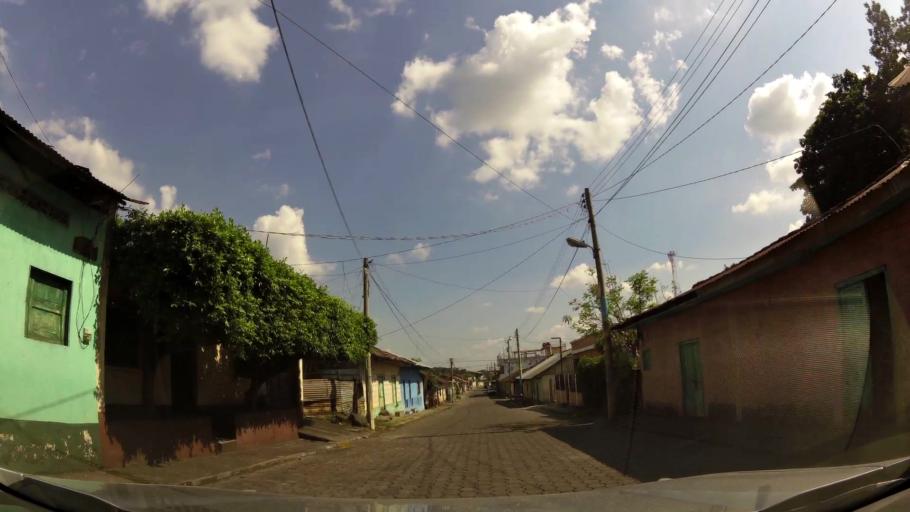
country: GT
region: Suchitepeque
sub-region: Municipio de Cuyotenango
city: Cuyotenango
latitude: 14.5416
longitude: -91.5756
